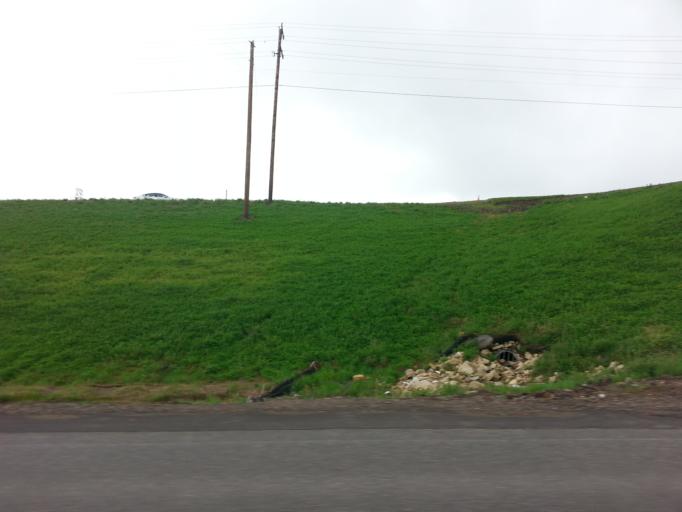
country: US
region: Minnesota
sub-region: Washington County
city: Oak Park Heights
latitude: 45.0355
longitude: -92.7969
